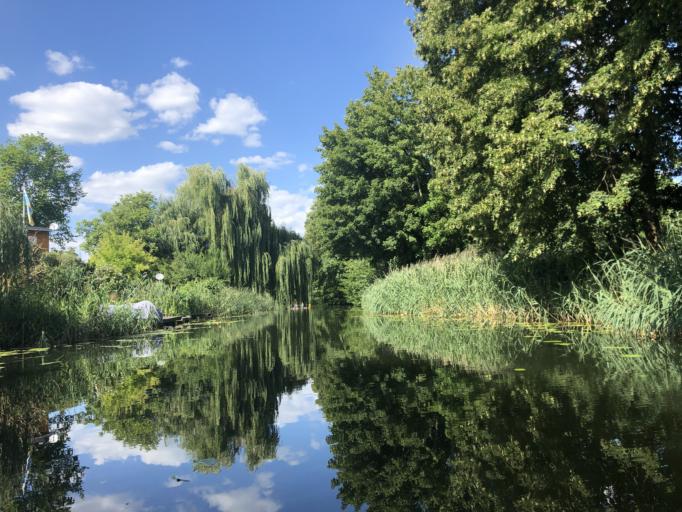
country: DE
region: Brandenburg
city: Mullrose
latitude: 52.2436
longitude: 14.4287
